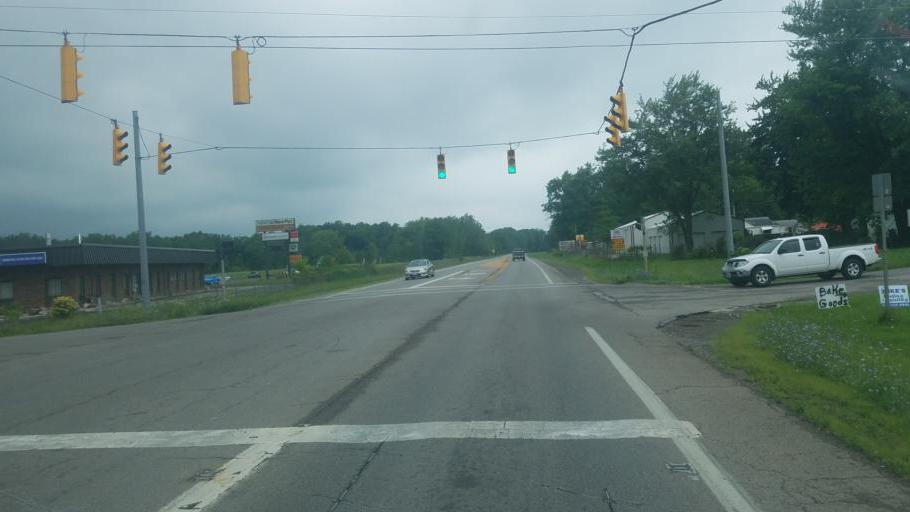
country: US
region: Ohio
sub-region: Logan County
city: Lakeview
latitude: 40.4793
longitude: -83.9076
